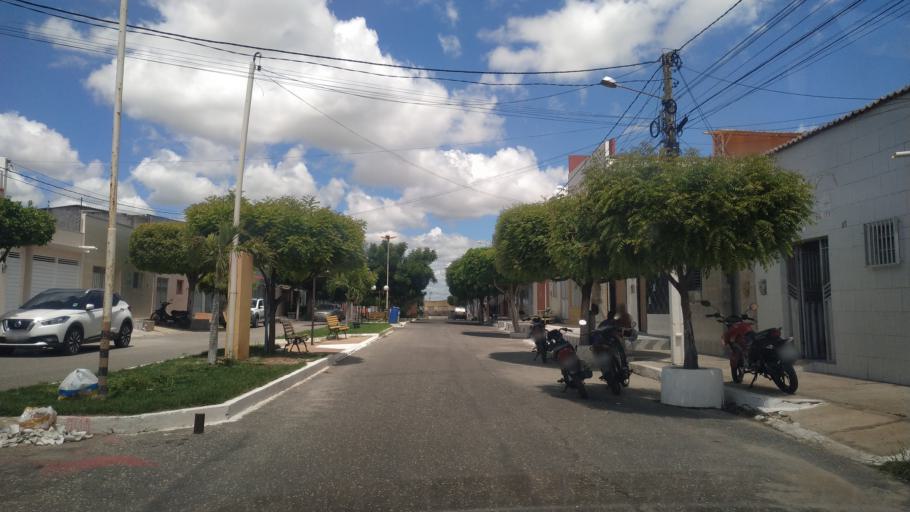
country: BR
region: Rio Grande do Norte
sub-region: Areia Branca
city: Areia Branca
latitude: -4.9565
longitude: -37.1312
